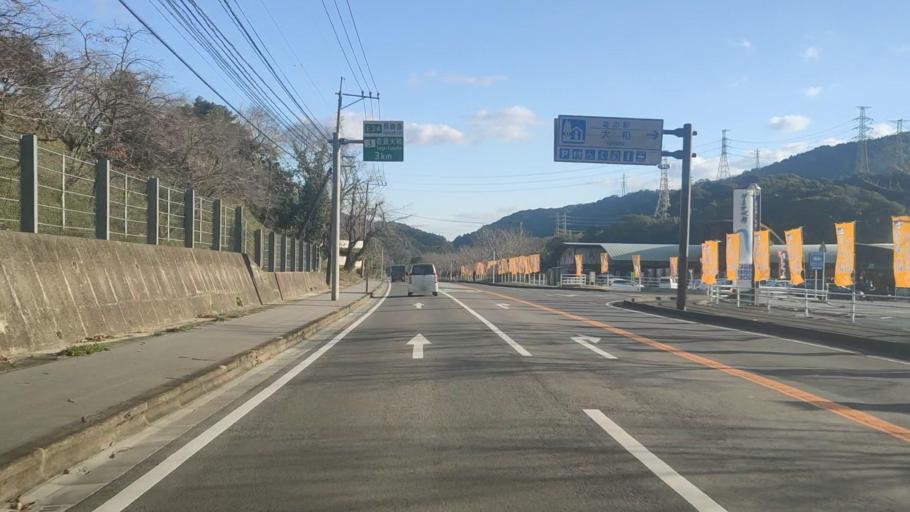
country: JP
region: Saga Prefecture
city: Saga-shi
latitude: 33.3401
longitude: 130.2575
